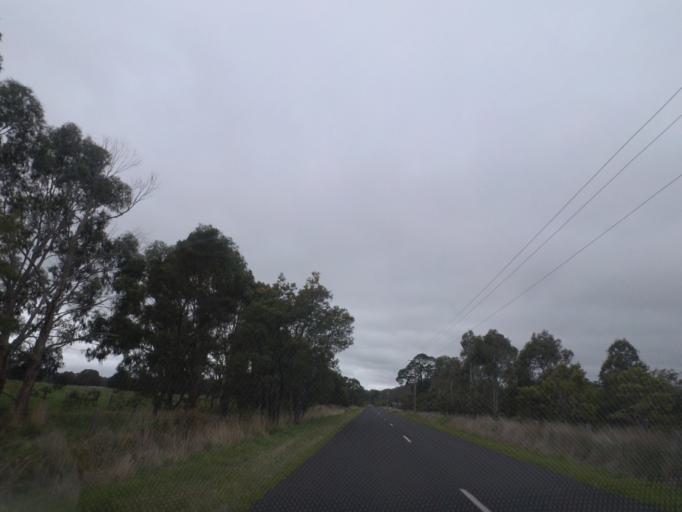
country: AU
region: Victoria
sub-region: Hume
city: Sunbury
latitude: -37.3259
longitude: 144.5802
